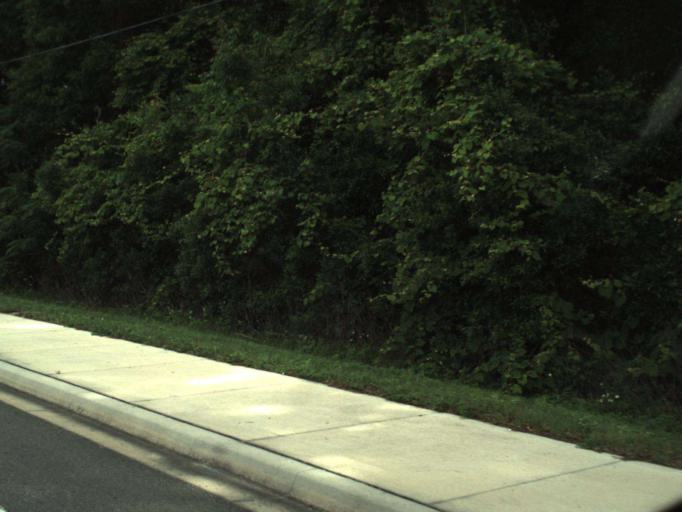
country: US
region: Florida
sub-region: Marion County
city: Silver Springs Shores
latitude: 29.1760
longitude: -82.0537
